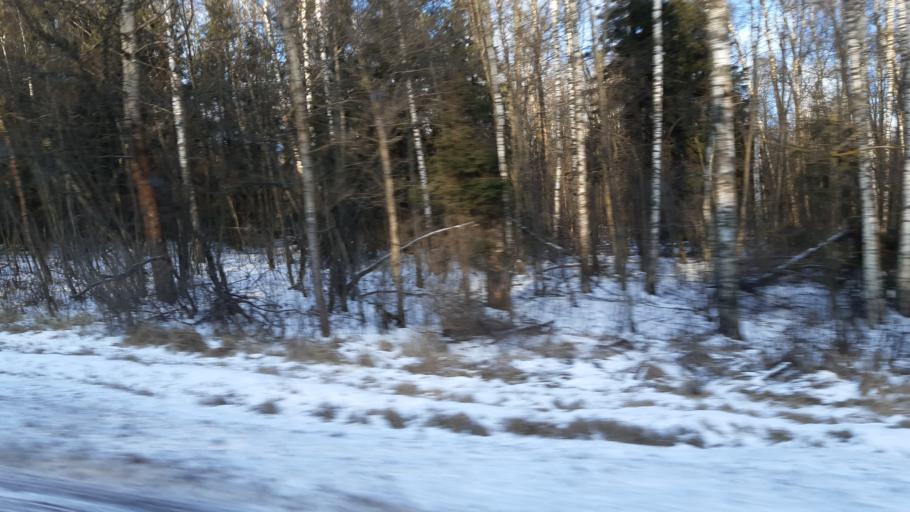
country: RU
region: Vladimir
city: Arsaki
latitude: 56.2918
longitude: 38.3789
